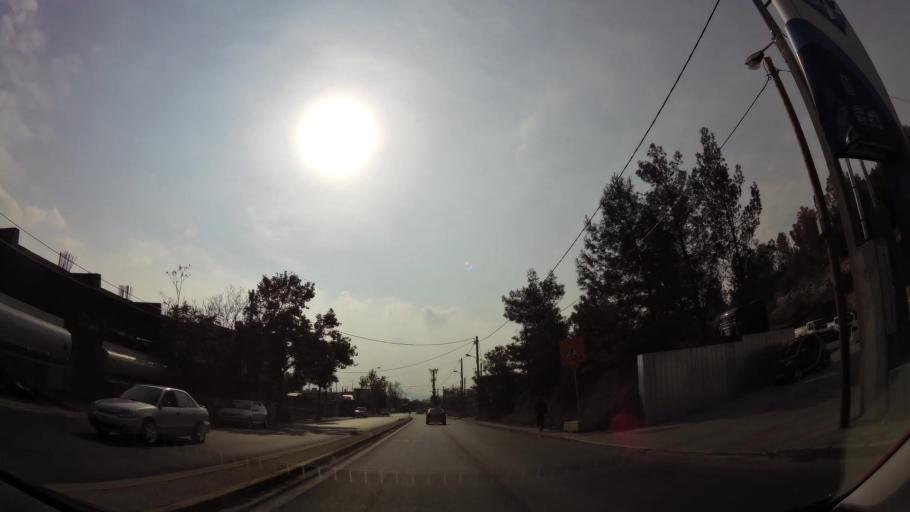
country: GR
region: Attica
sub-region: Nomarchia Dytikis Attikis
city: Zefyri
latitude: 38.0667
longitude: 23.7124
